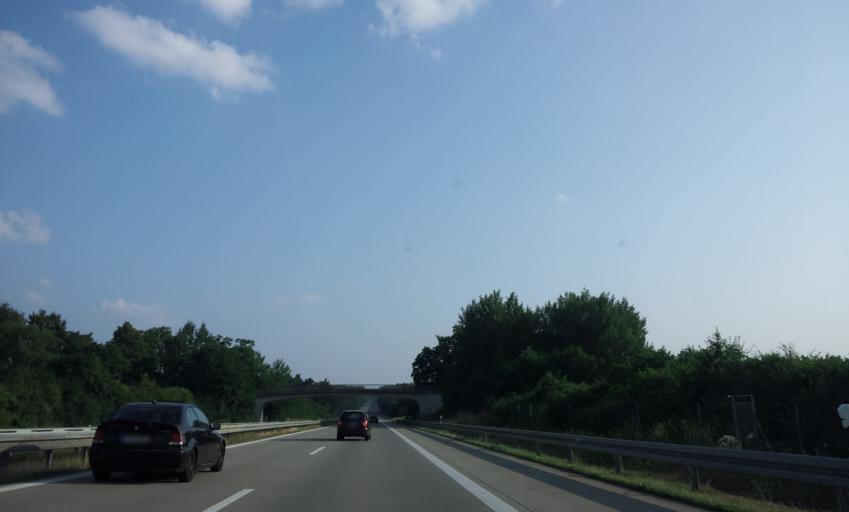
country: DE
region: Brandenburg
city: Althuttendorf
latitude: 53.0777
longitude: 13.8455
